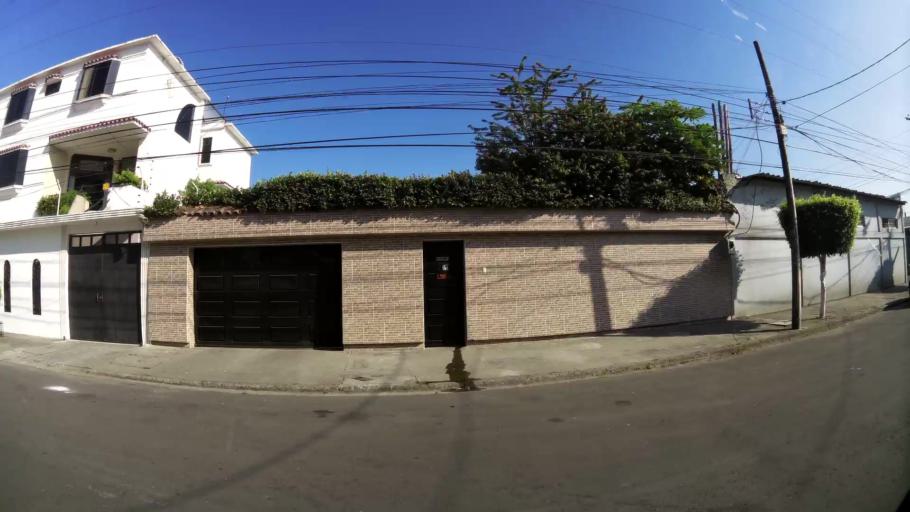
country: EC
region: Guayas
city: Eloy Alfaro
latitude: -2.1690
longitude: -79.8885
